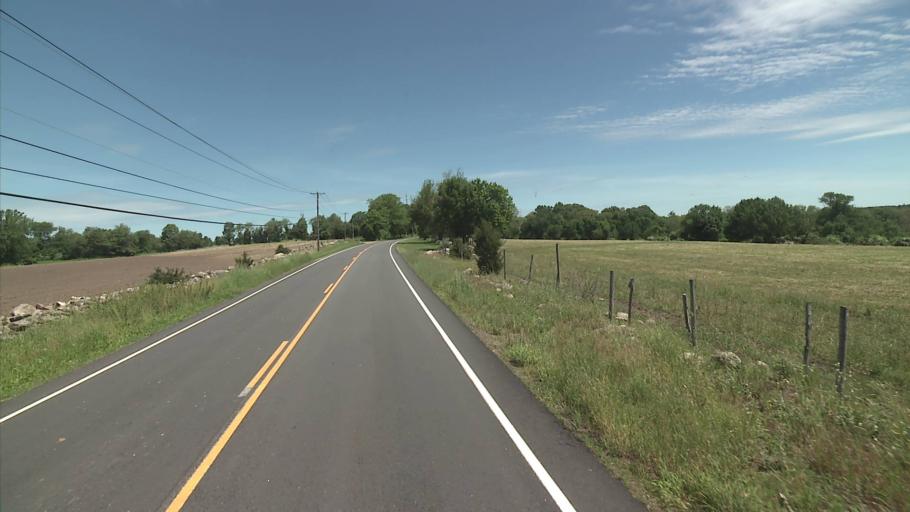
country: US
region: Connecticut
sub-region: Windham County
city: Moosup
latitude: 41.6567
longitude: -71.8478
